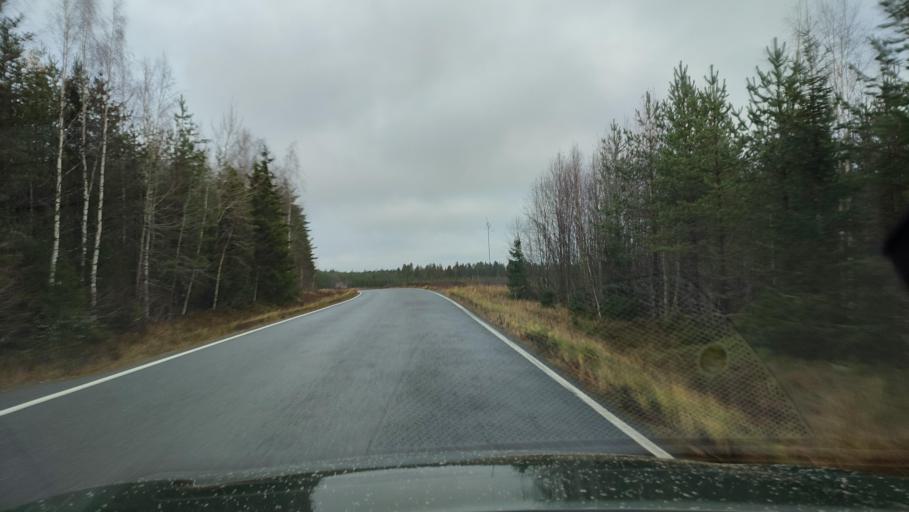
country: FI
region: Ostrobothnia
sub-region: Sydosterbotten
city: Kristinestad
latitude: 62.3371
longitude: 21.5163
